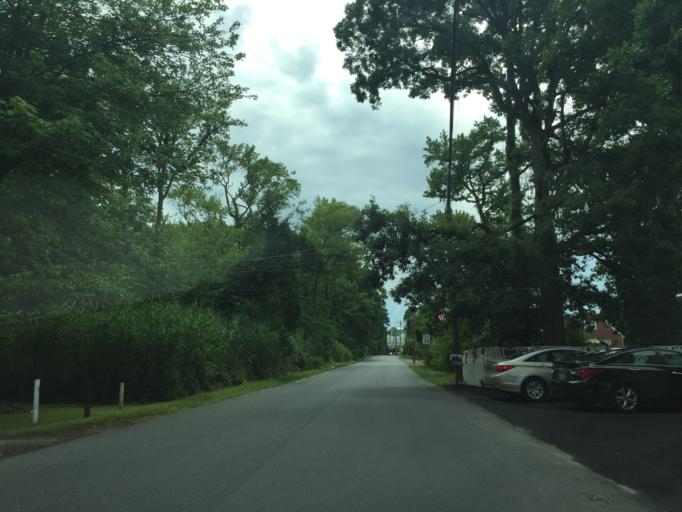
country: US
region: Maryland
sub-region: Baltimore County
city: Edgemere
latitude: 39.2730
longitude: -76.4541
